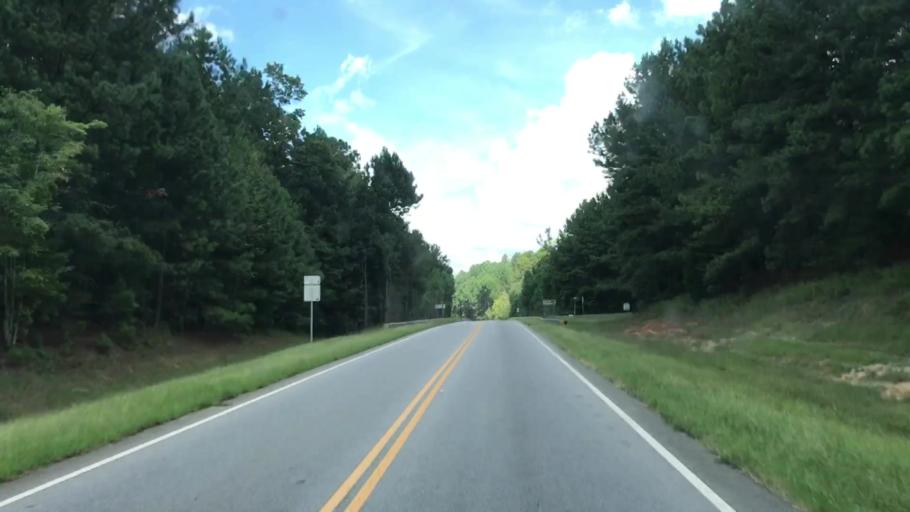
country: US
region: Georgia
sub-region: Greene County
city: Greensboro
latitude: 33.7130
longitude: -83.2917
